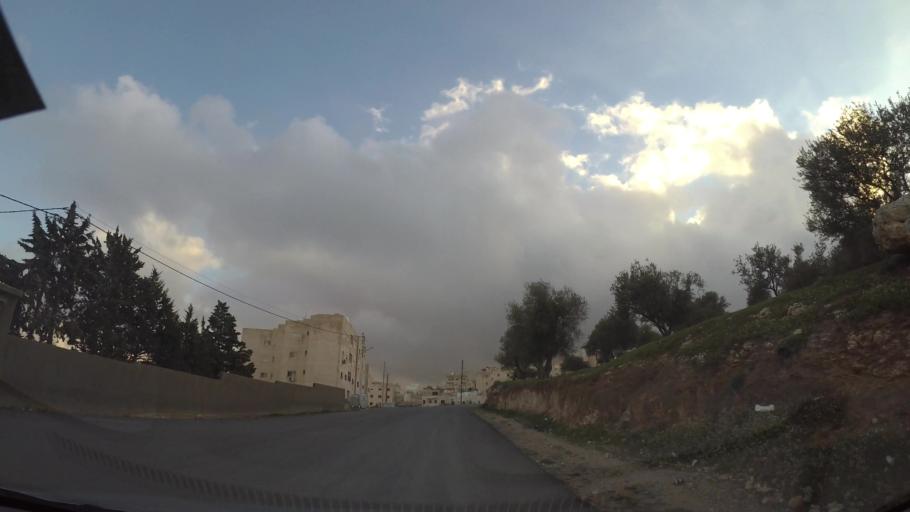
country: JO
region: Amman
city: Al Jubayhah
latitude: 32.0525
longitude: 35.8884
